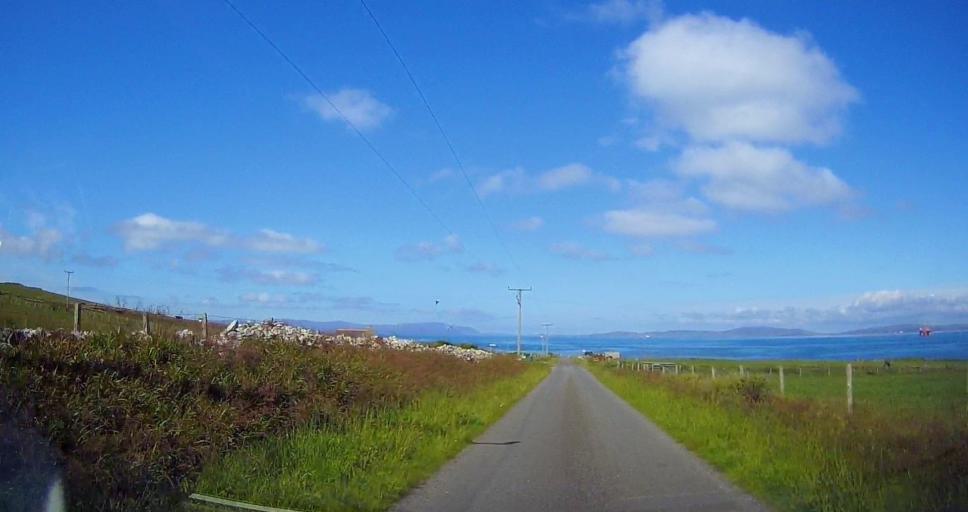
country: GB
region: Scotland
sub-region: Orkney Islands
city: Kirkwall
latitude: 58.8574
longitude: -2.9361
